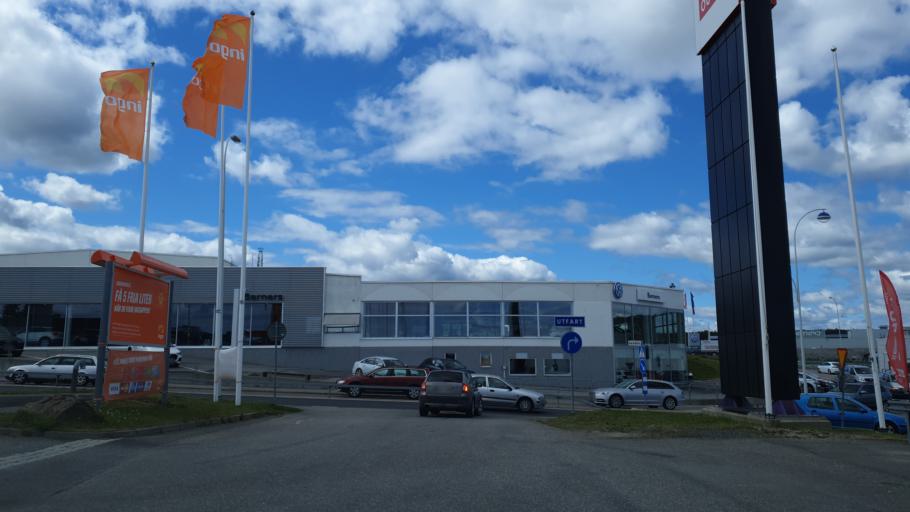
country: SE
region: Vaesternorrland
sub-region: Sundsvalls Kommun
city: Sundsbruk
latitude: 62.4426
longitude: 17.3327
